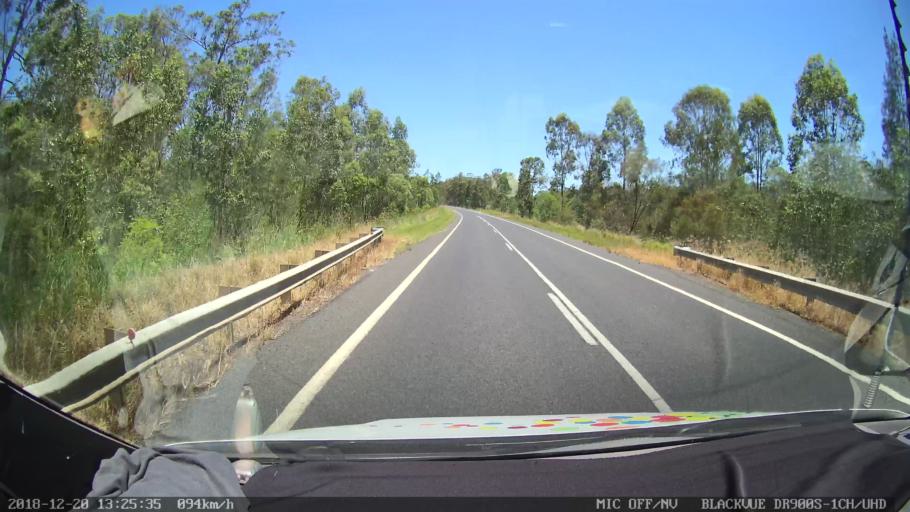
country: AU
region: New South Wales
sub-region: Richmond Valley
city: Casino
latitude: -29.1332
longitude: 152.9960
